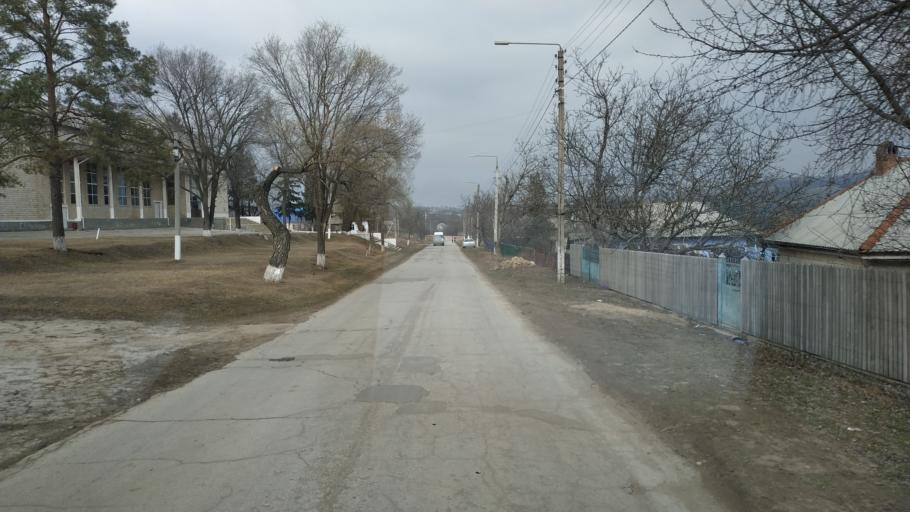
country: MD
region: Hincesti
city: Dancu
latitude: 46.8216
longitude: 28.2753
